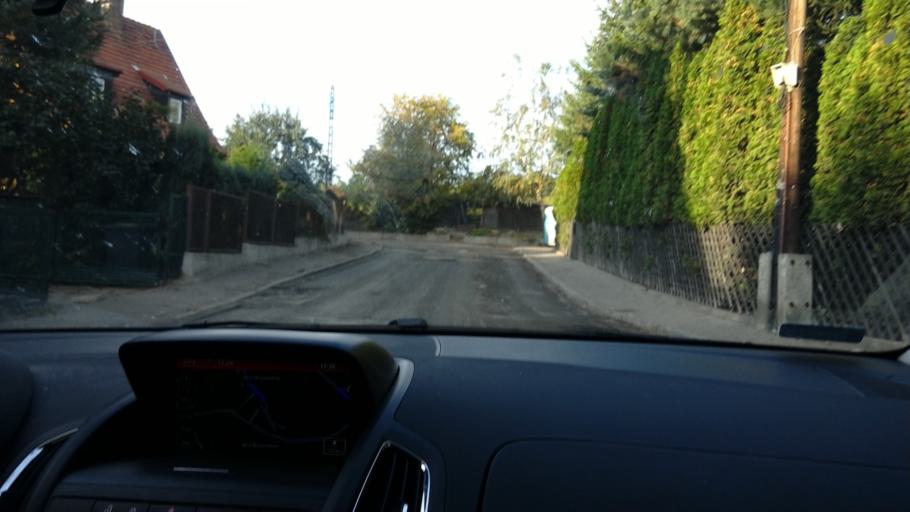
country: PL
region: Lower Silesian Voivodeship
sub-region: Jelenia Gora
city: Jelenia Gora
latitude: 50.8886
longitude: 15.7470
